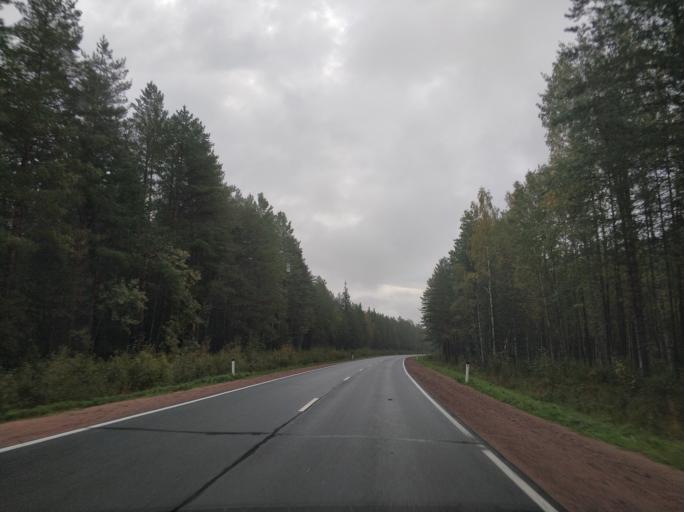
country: RU
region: Leningrad
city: Shcheglovo
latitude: 60.1029
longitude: 30.8172
